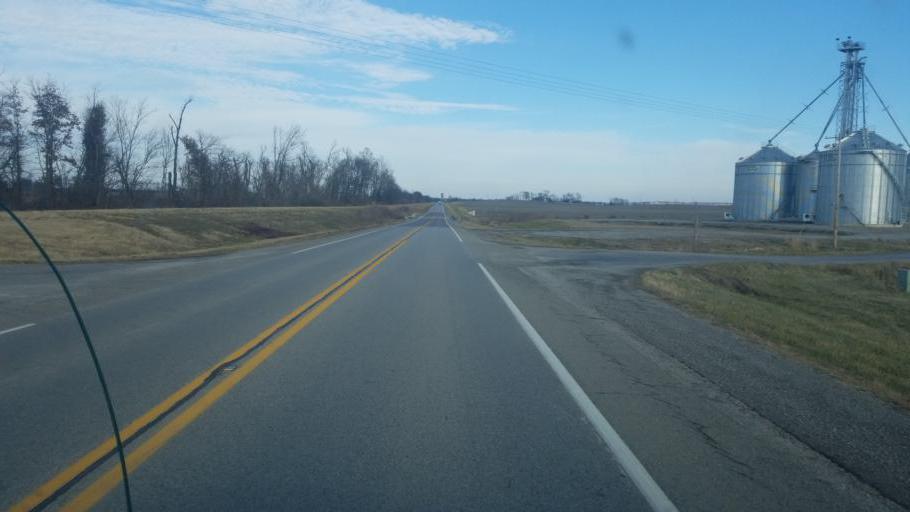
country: US
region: Illinois
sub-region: White County
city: Carmi
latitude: 38.1404
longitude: -88.0890
